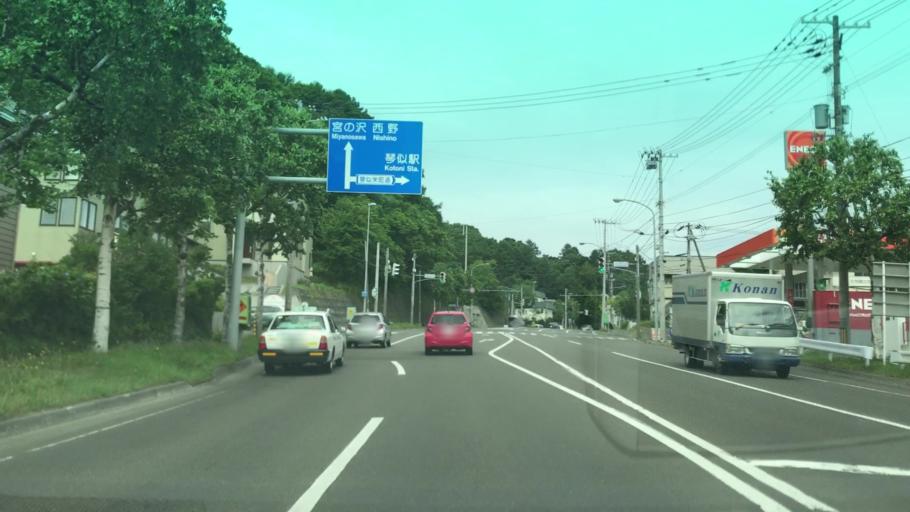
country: JP
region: Hokkaido
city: Sapporo
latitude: 43.0641
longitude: 141.2907
